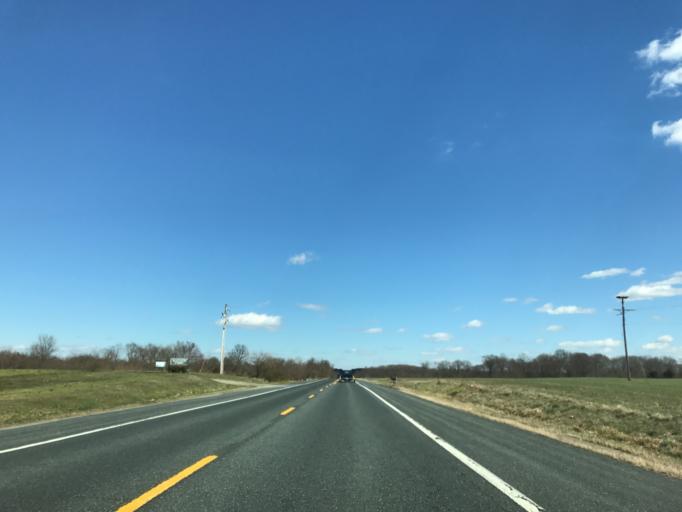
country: US
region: Maryland
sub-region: Queen Anne's County
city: Kingstown
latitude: 39.2082
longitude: -75.9931
